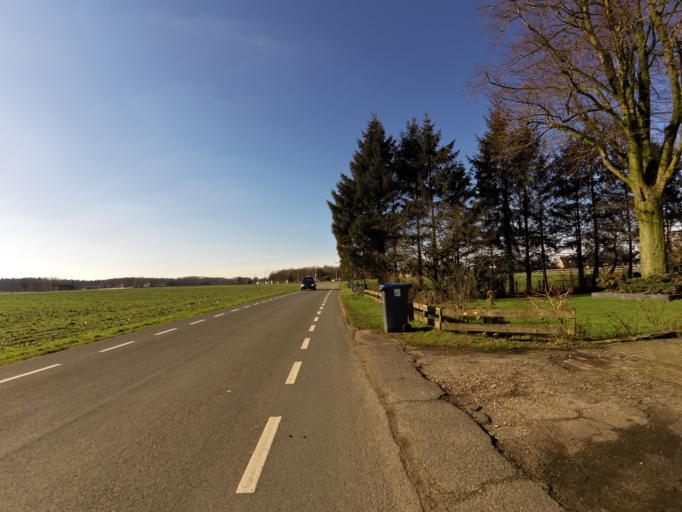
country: NL
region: Gelderland
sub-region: Gemeente Doesburg
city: Doesburg
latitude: 51.9629
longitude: 6.1974
